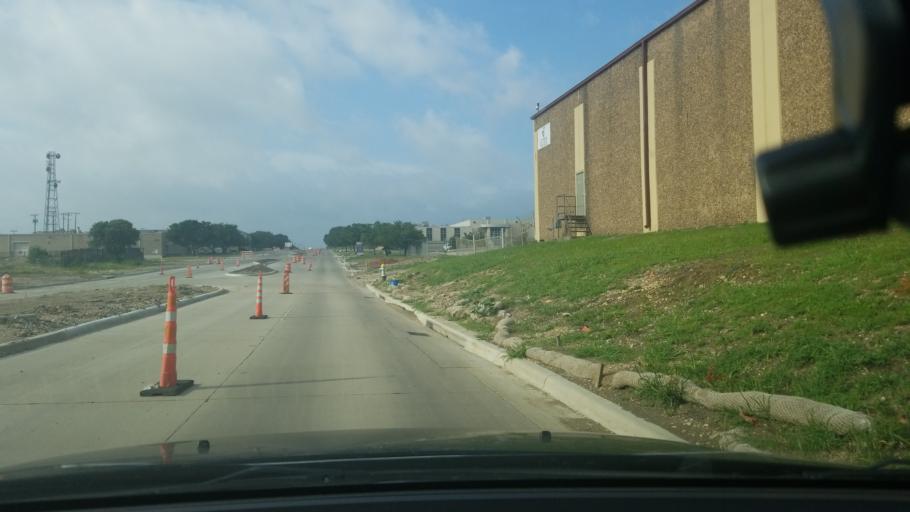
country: US
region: Texas
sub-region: Dallas County
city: Mesquite
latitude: 32.7764
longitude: -96.6467
